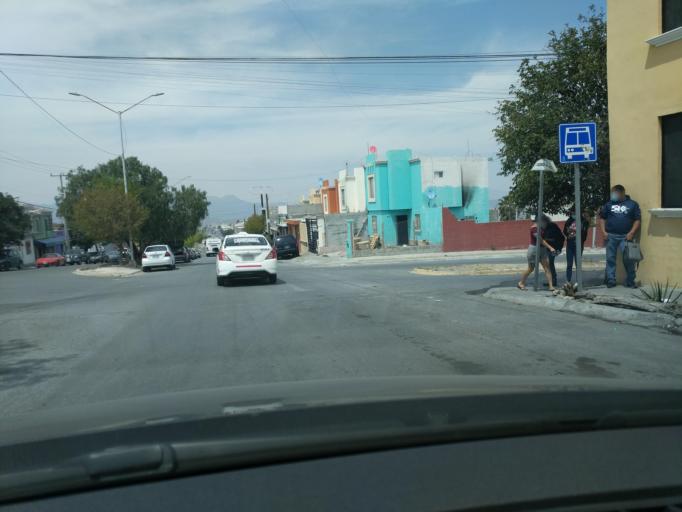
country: MX
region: Coahuila
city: Saltillo
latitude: 25.3504
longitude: -101.0112
